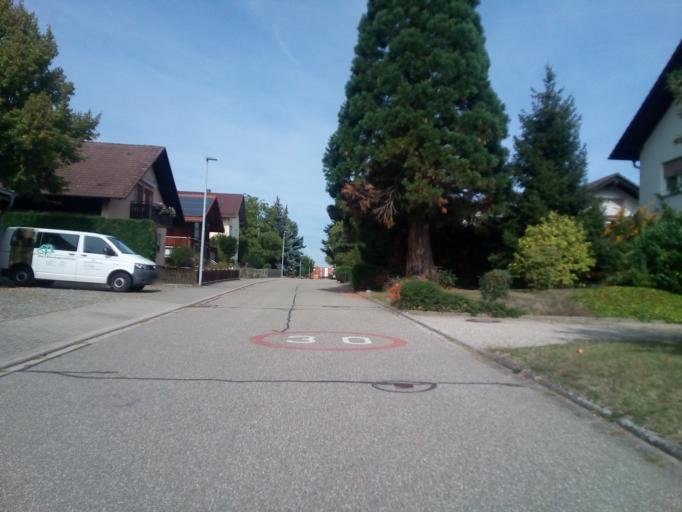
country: DE
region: Baden-Wuerttemberg
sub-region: Karlsruhe Region
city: Ottenhofen
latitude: 48.7407
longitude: 8.1374
